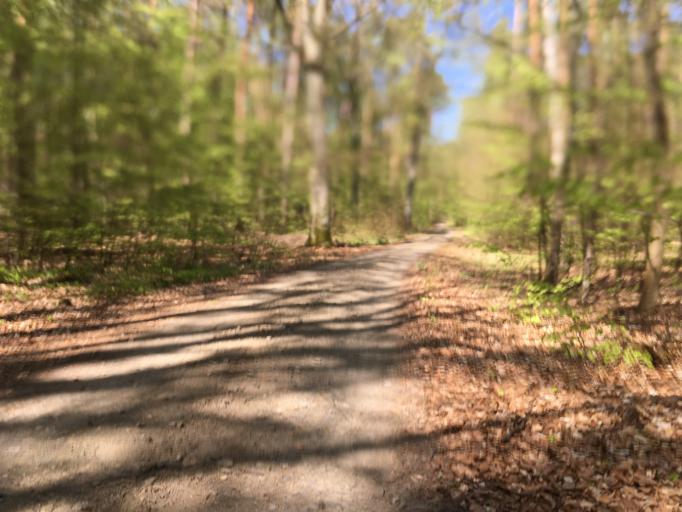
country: DE
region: Brandenburg
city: Wandlitz
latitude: 52.7555
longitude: 13.4967
